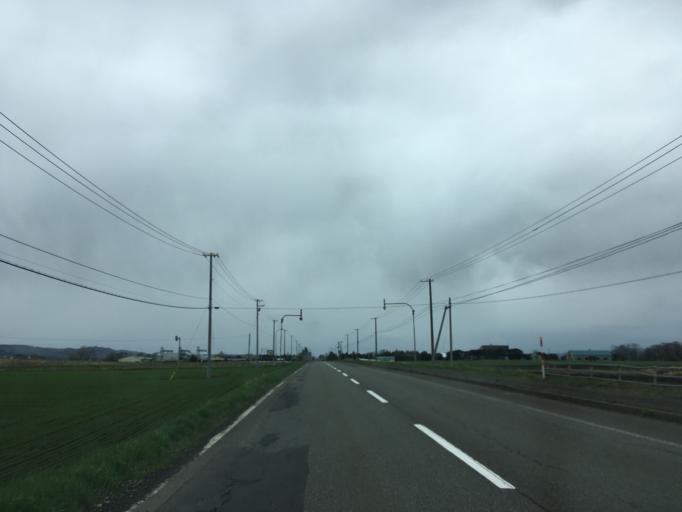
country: JP
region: Hokkaido
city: Chitose
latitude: 42.9270
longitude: 141.8077
